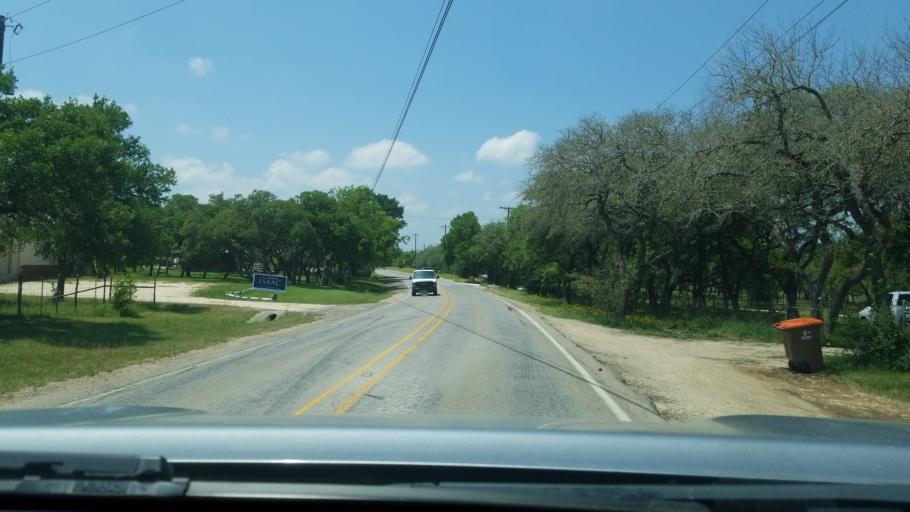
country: US
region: Texas
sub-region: Hays County
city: Woodcreek
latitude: 30.0325
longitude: -98.1735
